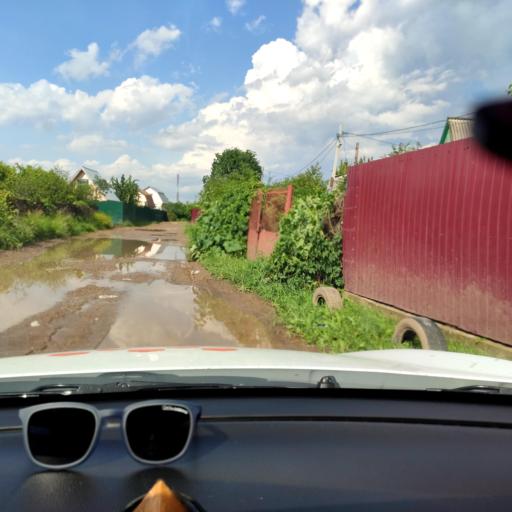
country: RU
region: Tatarstan
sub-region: Zelenodol'skiy Rayon
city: Vasil'yevo
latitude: 55.8239
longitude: 48.7241
